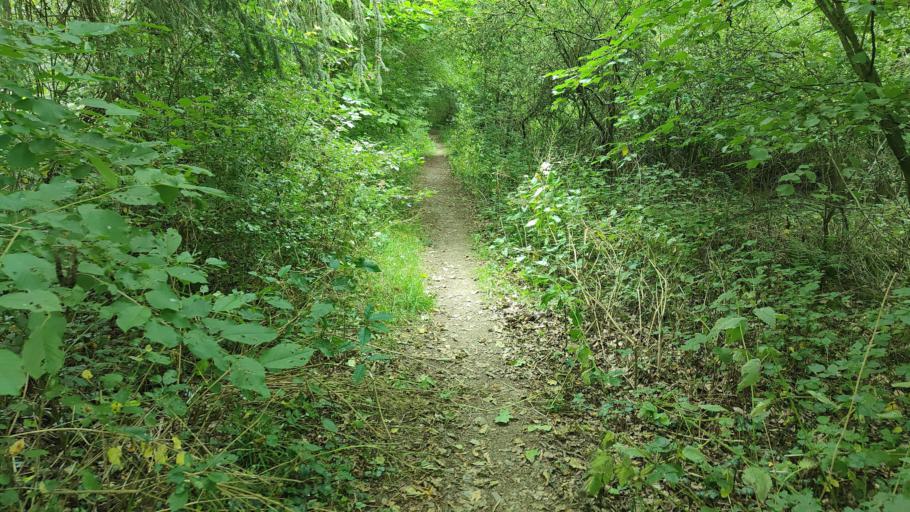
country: BE
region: Wallonia
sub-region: Province du Hainaut
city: Chimay
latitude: 50.0526
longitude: 4.3869
